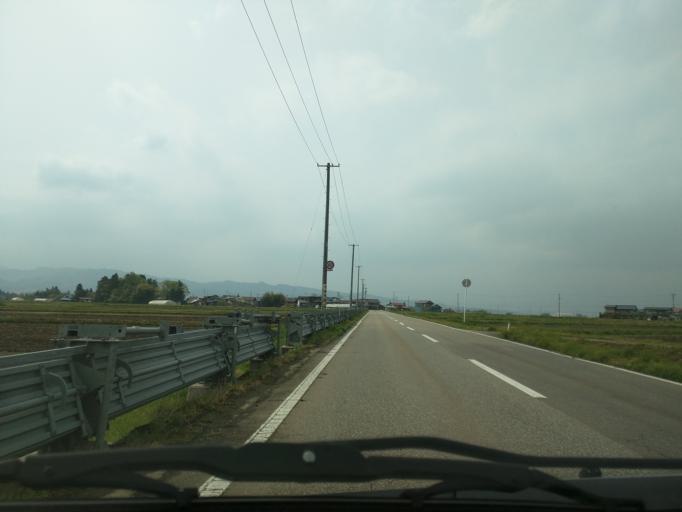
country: JP
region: Fukushima
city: Kitakata
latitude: 37.4386
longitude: 139.8604
